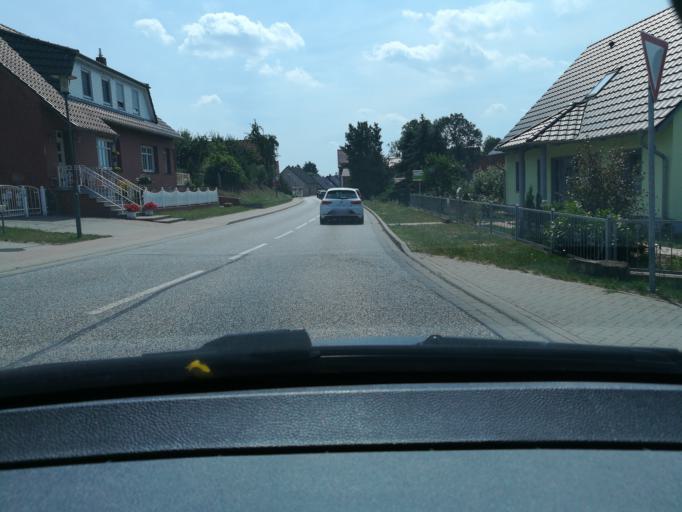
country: DE
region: Brandenburg
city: Wittstock
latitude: 53.0731
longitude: 12.4728
